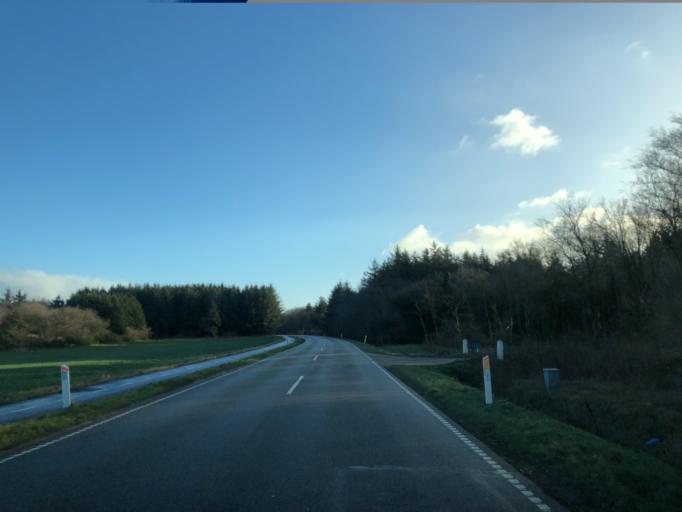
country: DK
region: Central Jutland
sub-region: Holstebro Kommune
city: Ulfborg
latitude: 56.1972
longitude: 8.2850
